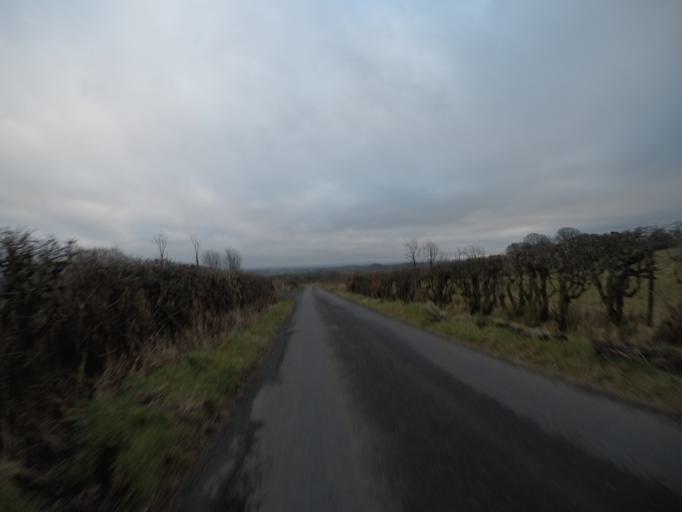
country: GB
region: Scotland
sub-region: North Ayrshire
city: Dalry
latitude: 55.7176
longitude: -4.7567
